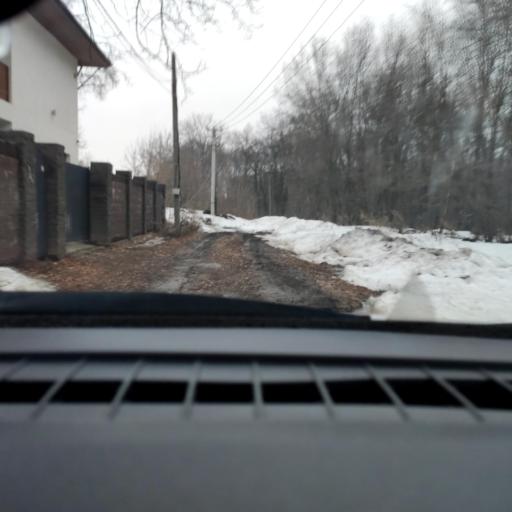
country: RU
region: Samara
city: Novosemeykino
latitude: 53.3288
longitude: 50.2789
